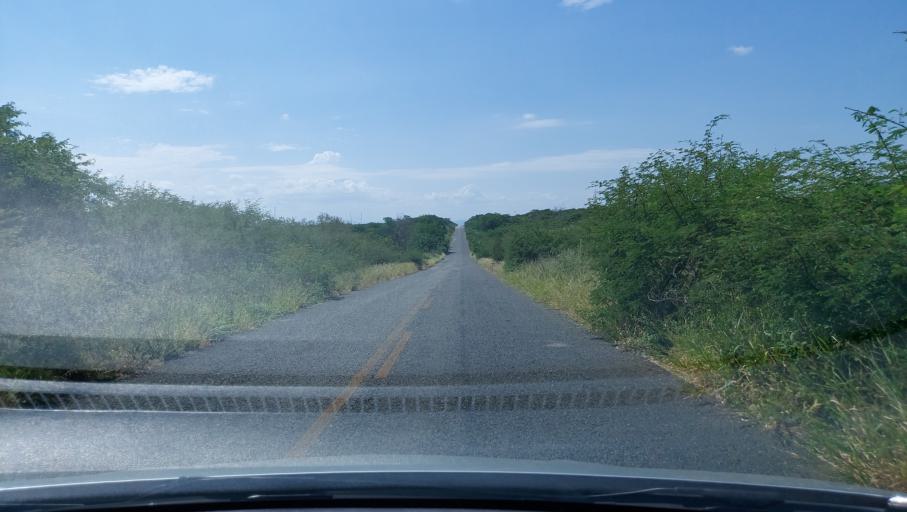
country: BR
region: Bahia
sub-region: Oliveira Dos Brejinhos
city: Beira Rio
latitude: -12.1723
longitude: -42.5453
